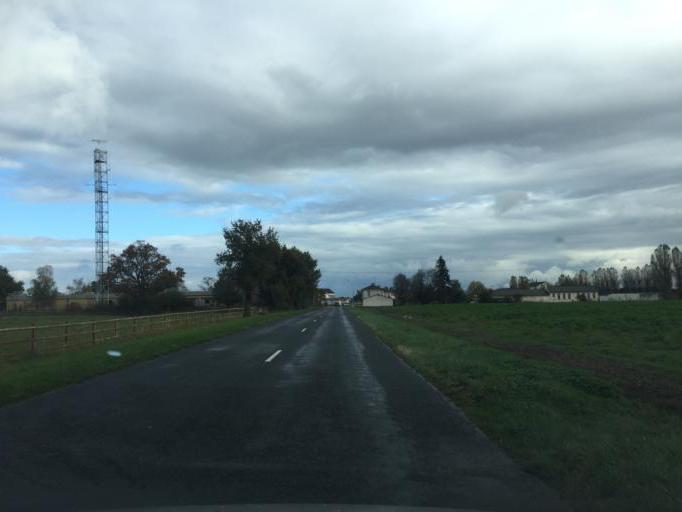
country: FR
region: Rhone-Alpes
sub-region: Departement de l'Ain
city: Saint-Andre-de-Corcy
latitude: 45.9235
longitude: 4.9405
